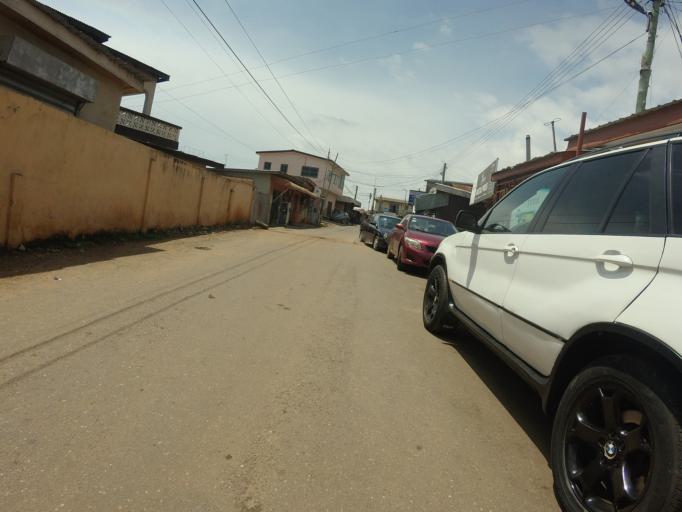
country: GH
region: Greater Accra
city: Accra
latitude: 5.5890
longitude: -0.2066
